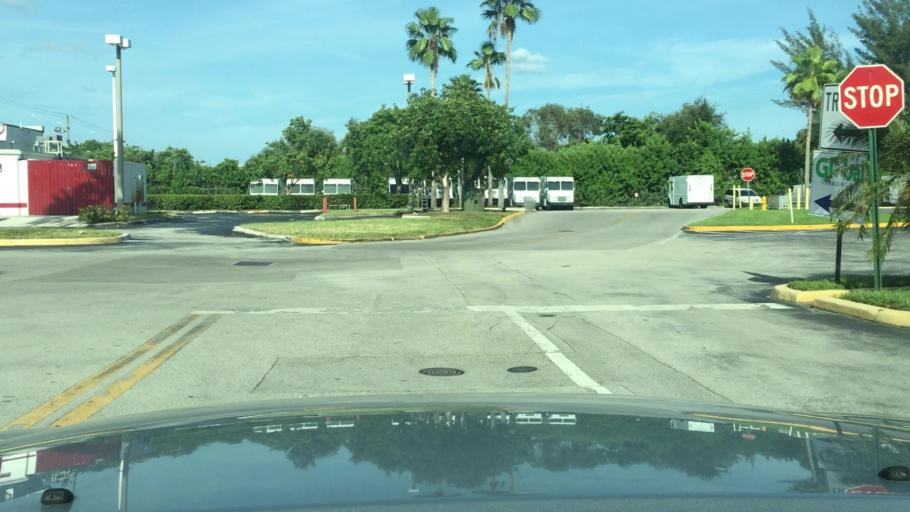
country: US
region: Florida
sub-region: Miami-Dade County
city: Virginia Gardens
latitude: 25.7965
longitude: -80.3186
